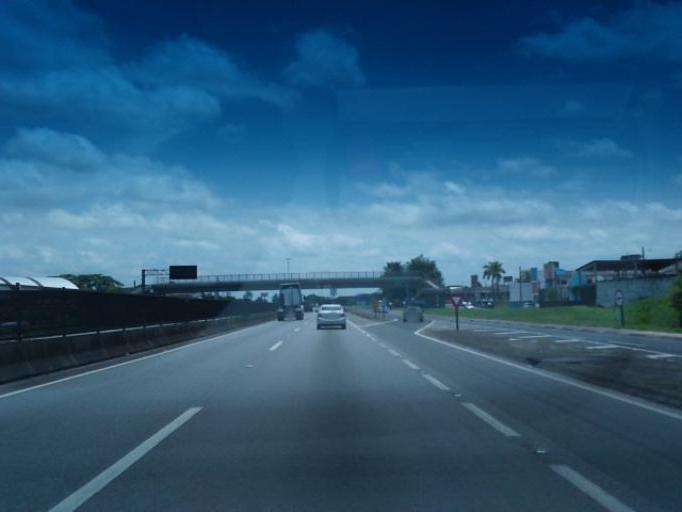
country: BR
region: Sao Paulo
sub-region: Registro
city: Registro
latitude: -24.4999
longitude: -47.8445
